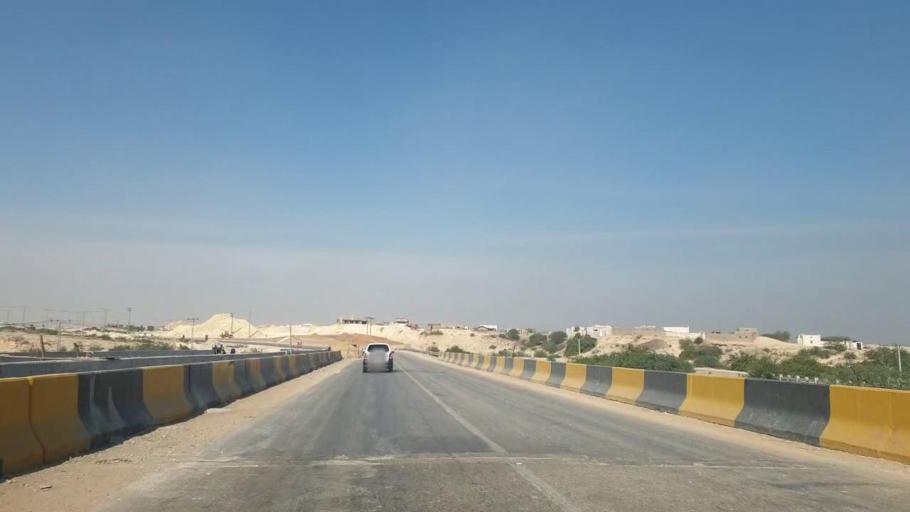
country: PK
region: Sindh
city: Hala
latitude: 25.7324
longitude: 68.2927
